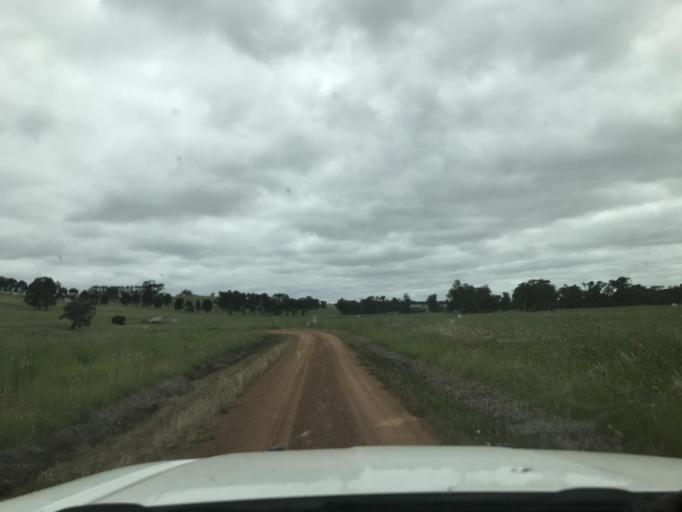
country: AU
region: South Australia
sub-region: Wattle Range
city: Penola
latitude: -37.3573
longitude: 141.2121
